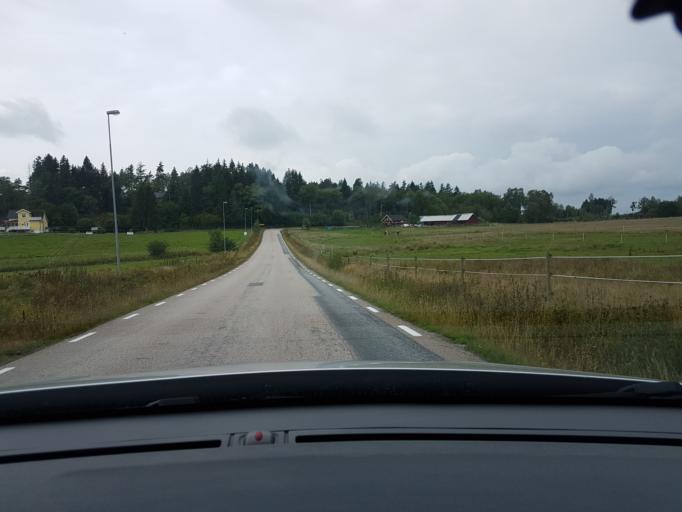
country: SE
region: Vaestra Goetaland
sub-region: Ale Kommun
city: Alvangen
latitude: 57.9178
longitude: 12.1369
